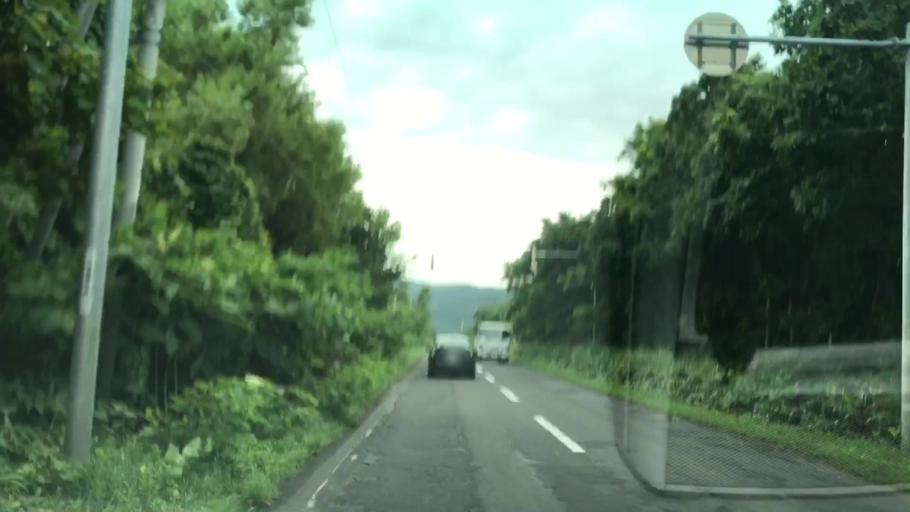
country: JP
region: Hokkaido
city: Iwanai
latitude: 42.8881
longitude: 140.3739
